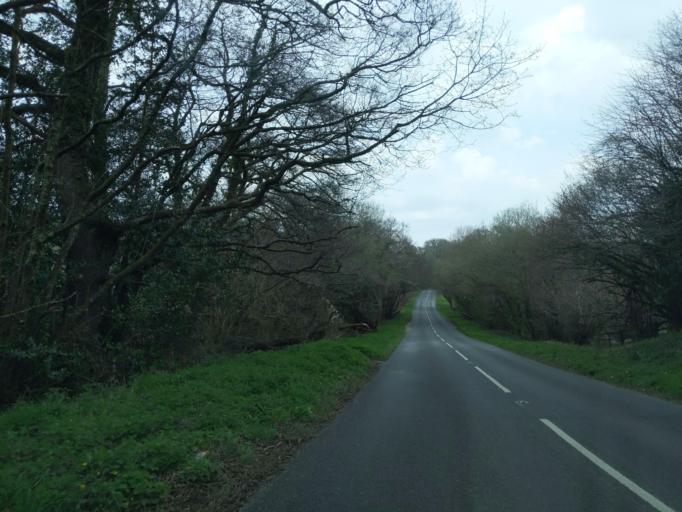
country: GB
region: England
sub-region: Devon
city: Ashburton
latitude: 50.6488
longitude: -3.8109
